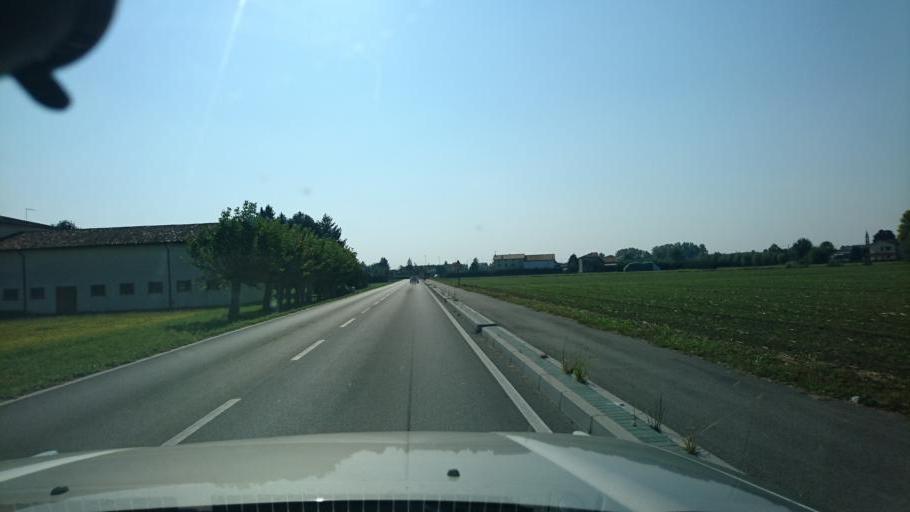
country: IT
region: Veneto
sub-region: Provincia di Padova
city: Gazzo
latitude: 45.5629
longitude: 11.7106
